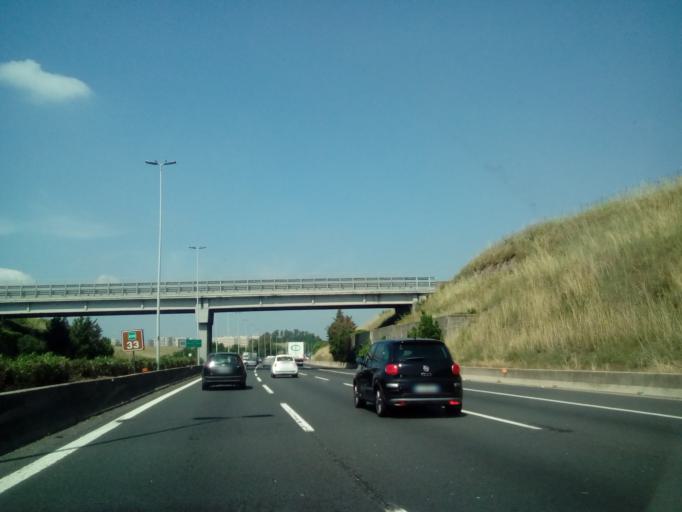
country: IT
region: Latium
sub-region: Citta metropolitana di Roma Capitale
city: Selcetta
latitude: 41.7942
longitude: 12.5120
